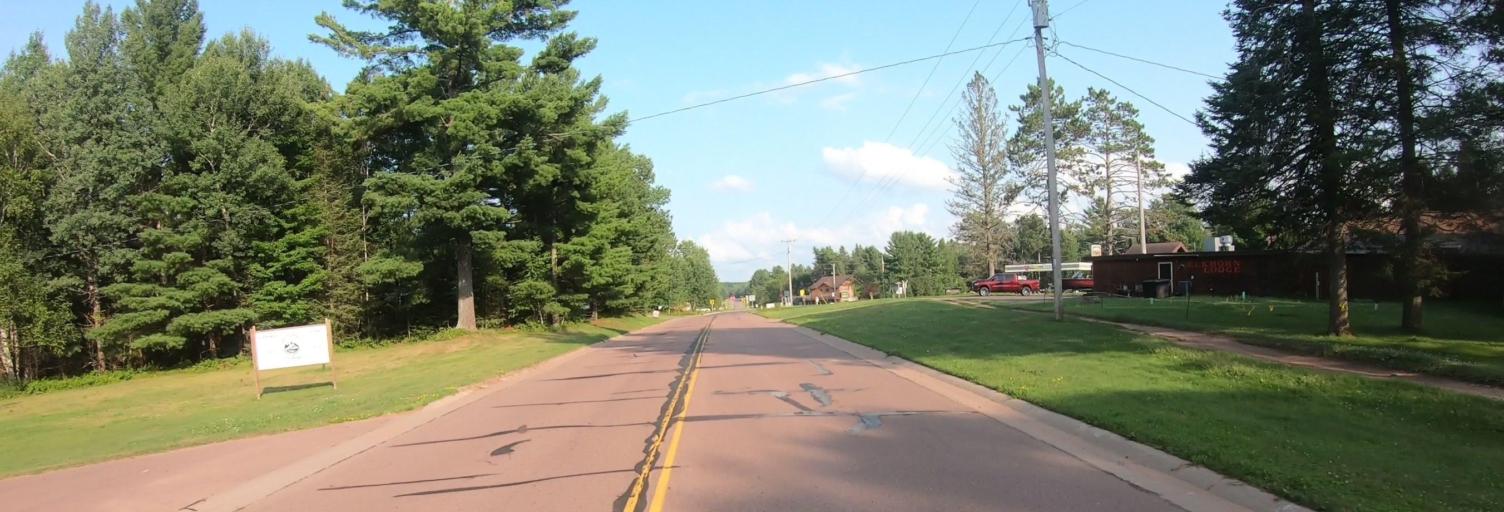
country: US
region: Wisconsin
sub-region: Ashland County
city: Ashland
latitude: 46.1737
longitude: -90.9117
